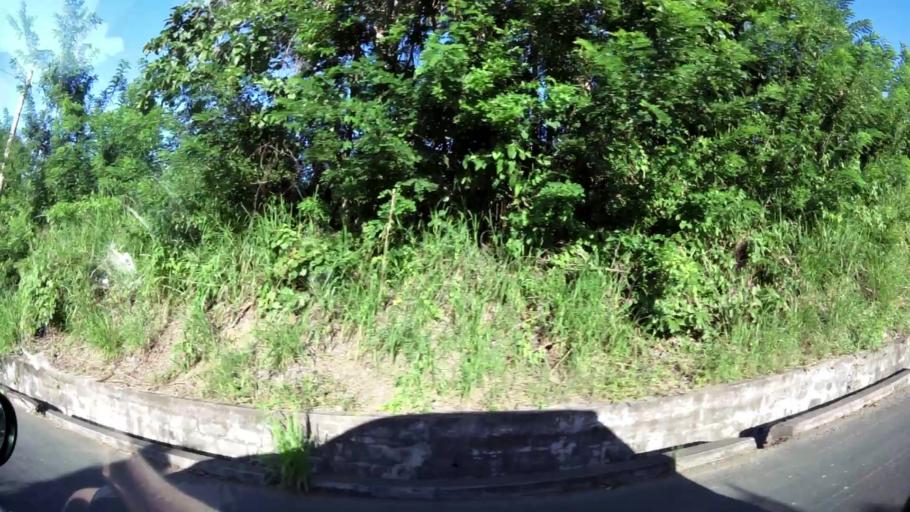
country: TT
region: Tobago
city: Scarborough
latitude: 11.2108
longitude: -60.7633
